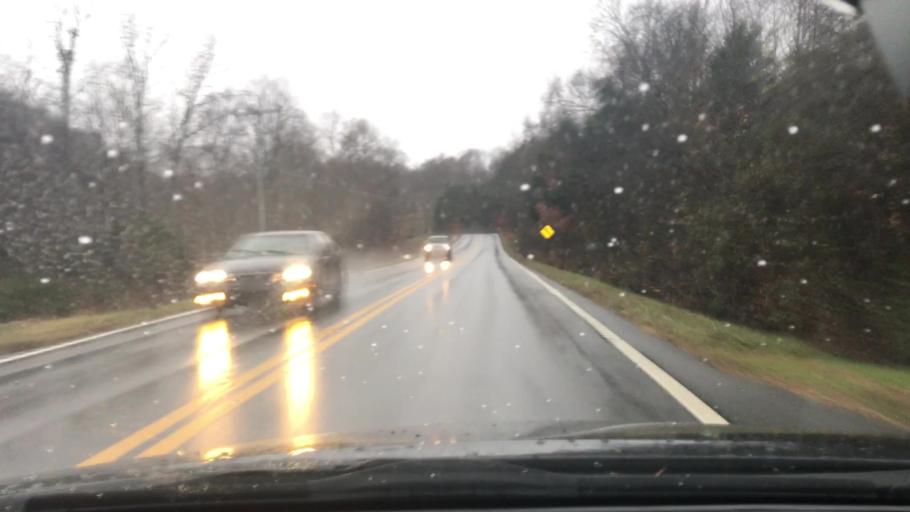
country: US
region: Tennessee
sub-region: Cheatham County
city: Ashland City
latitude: 36.2793
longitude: -87.1422
